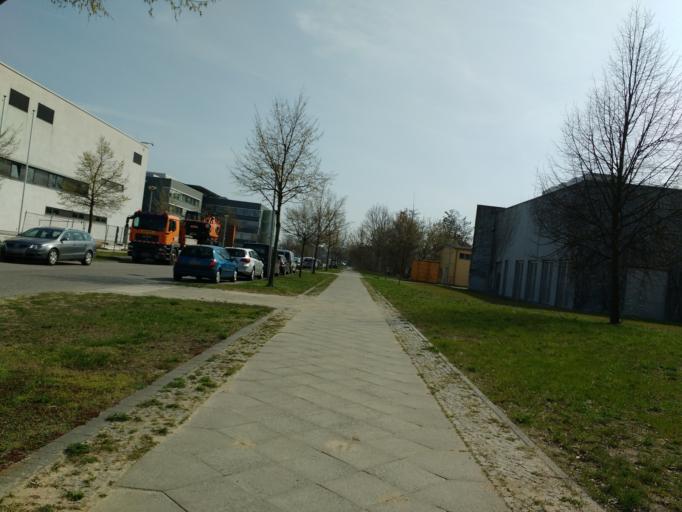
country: DE
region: Berlin
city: Adlershof
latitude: 52.4278
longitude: 13.5341
